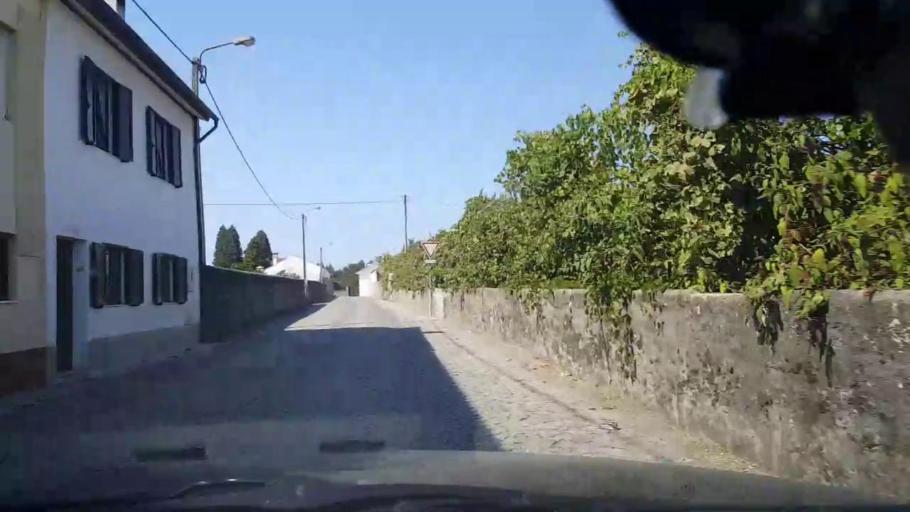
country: PT
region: Porto
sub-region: Vila do Conde
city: Arvore
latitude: 41.3866
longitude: -8.7058
